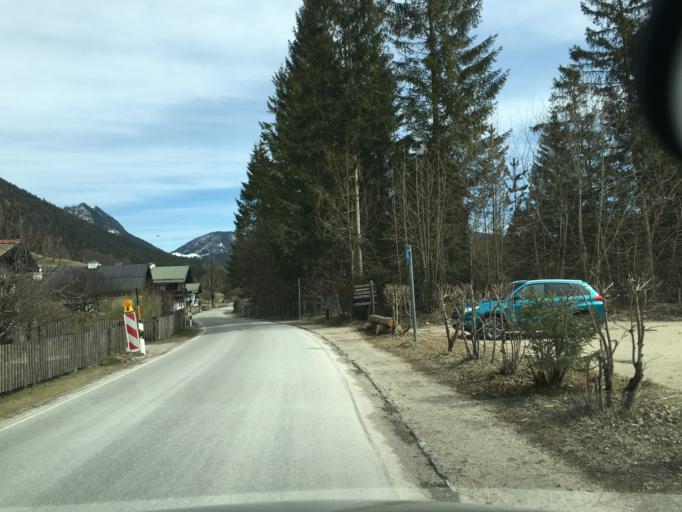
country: DE
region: Bavaria
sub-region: Upper Bavaria
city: Ramsau
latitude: 47.5993
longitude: 12.8434
